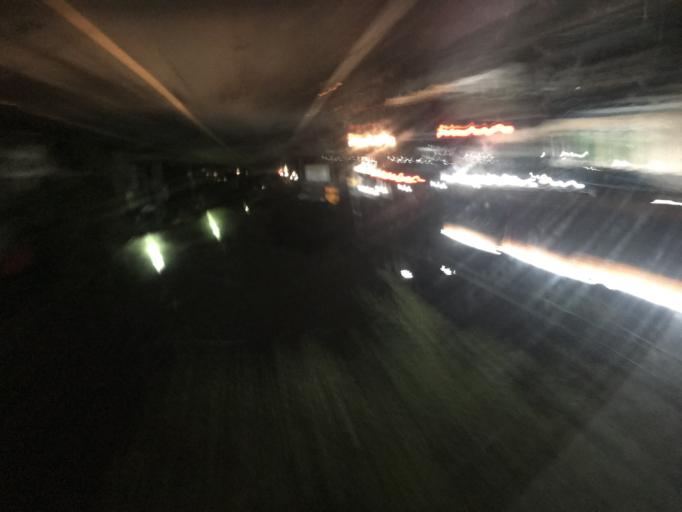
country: TH
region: Bangkok
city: Taling Chan
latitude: 13.7717
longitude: 100.4507
